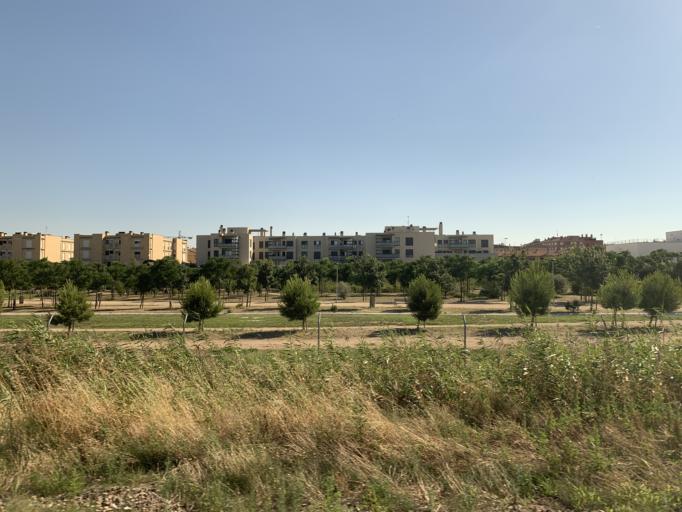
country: ES
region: Aragon
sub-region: Provincia de Zaragoza
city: Utebo
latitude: 41.7083
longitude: -0.9943
